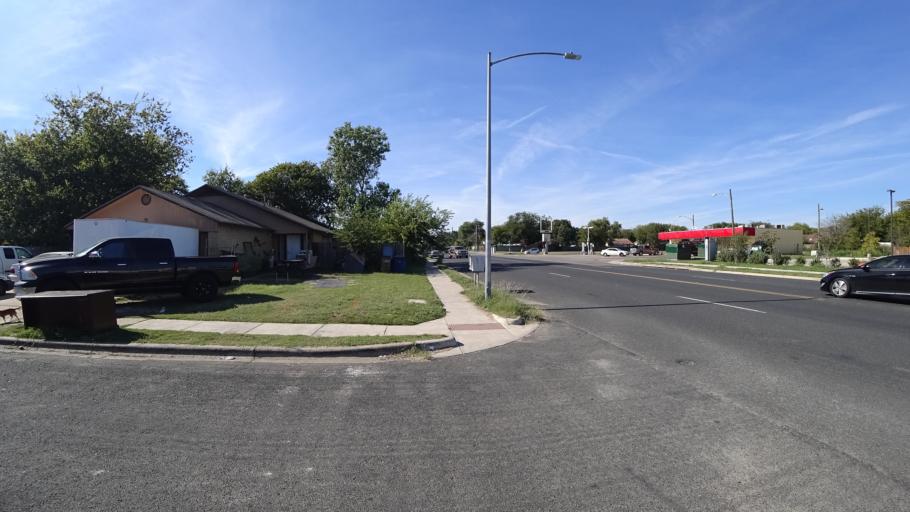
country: US
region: Texas
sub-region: Travis County
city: Austin
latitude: 30.1965
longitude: -97.7435
